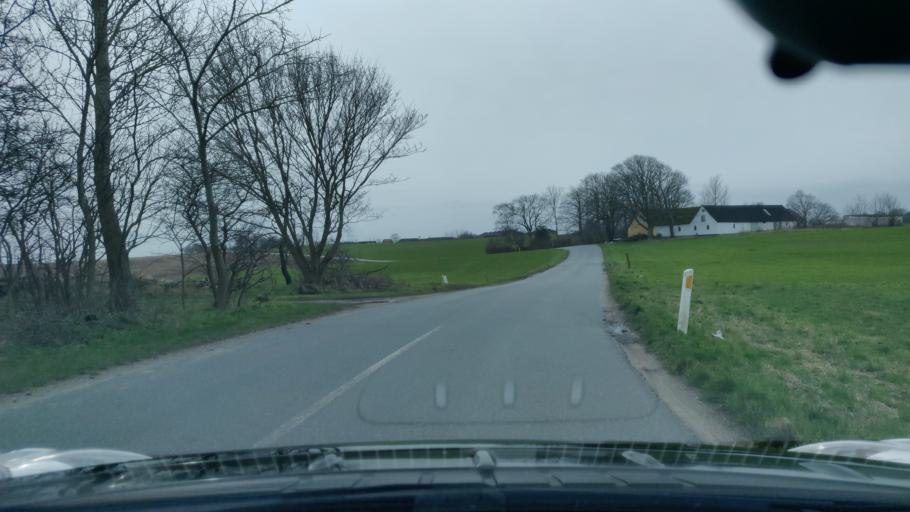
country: DK
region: Zealand
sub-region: Odsherred Kommune
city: Hojby
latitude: 55.9194
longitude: 11.5965
